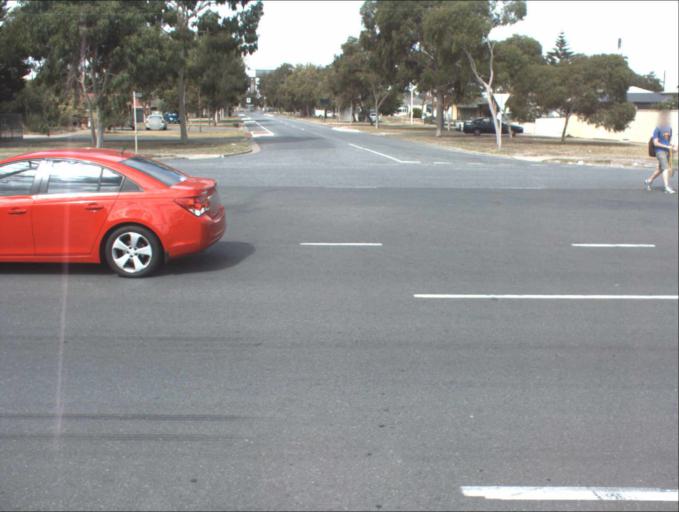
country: AU
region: South Australia
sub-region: Port Adelaide Enfield
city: Birkenhead
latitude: -34.8011
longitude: 138.5012
